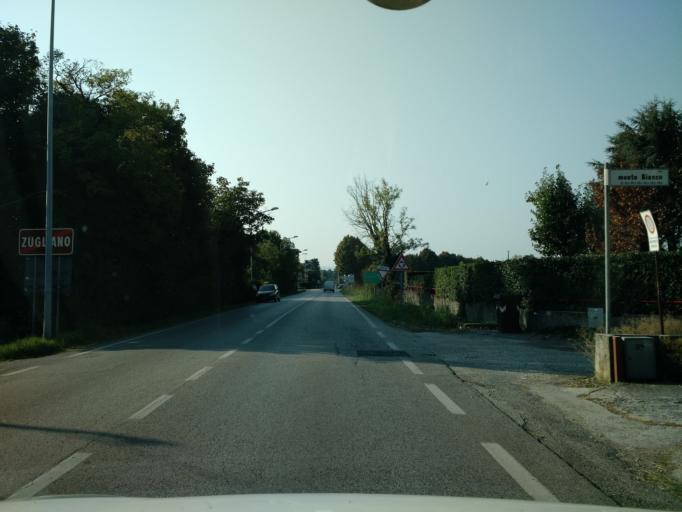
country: IT
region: Veneto
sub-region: Provincia di Vicenza
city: Grumolo Pedemonte
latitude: 45.7167
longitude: 11.4887
